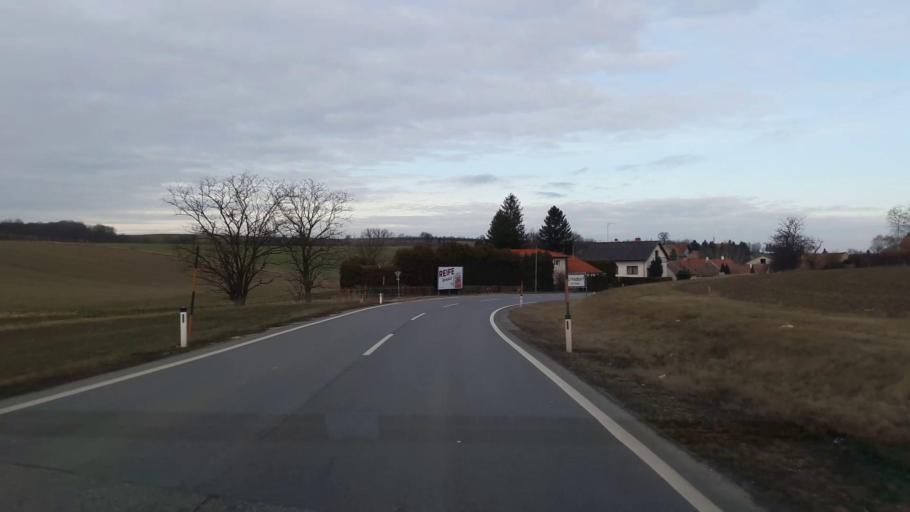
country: AT
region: Lower Austria
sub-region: Politischer Bezirk Mistelbach
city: Staatz
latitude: 48.6575
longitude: 16.4970
